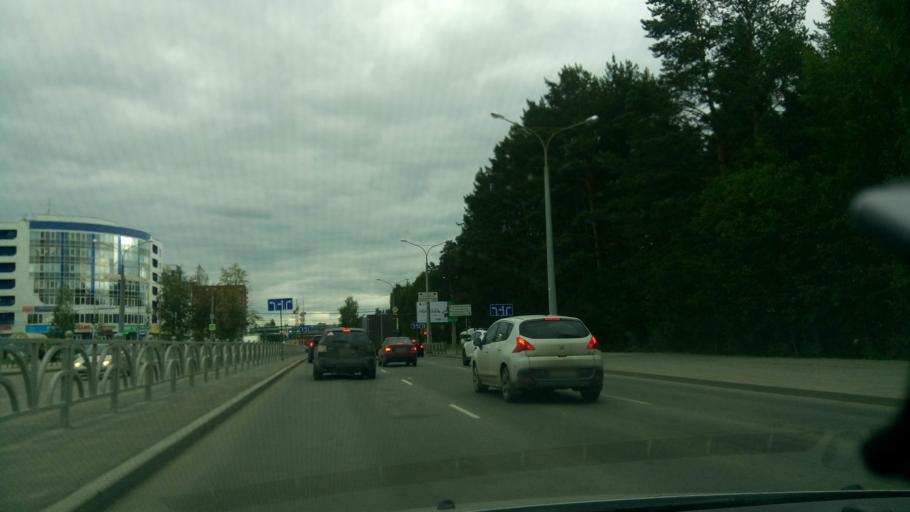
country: RU
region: Sverdlovsk
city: Sovkhoznyy
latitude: 56.7771
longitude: 60.5504
